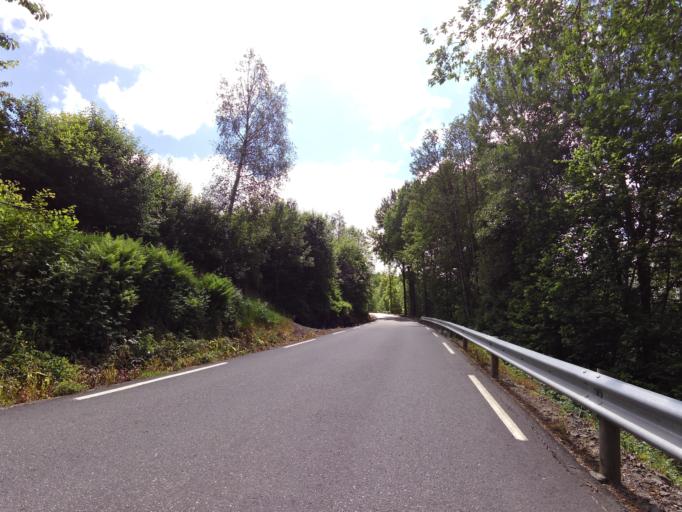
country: NO
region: Vest-Agder
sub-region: Kvinesdal
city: Liknes
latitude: 58.2901
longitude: 6.9391
